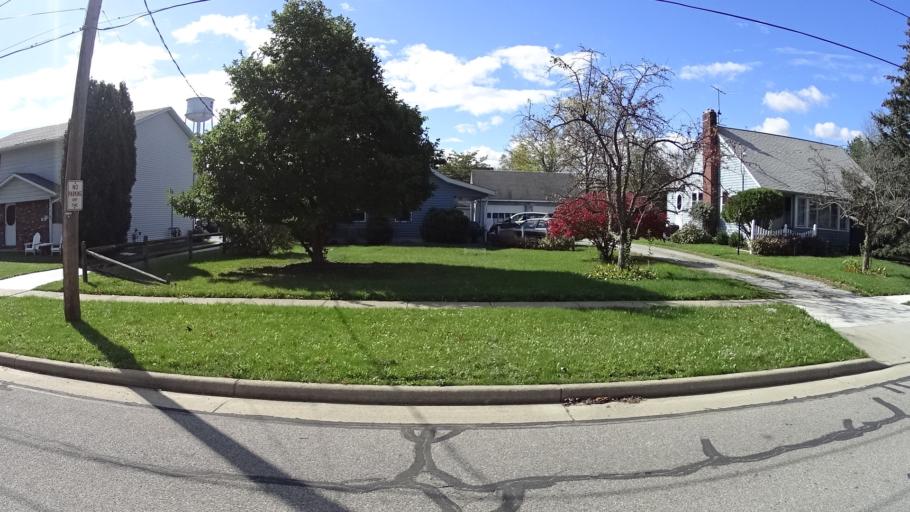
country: US
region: Ohio
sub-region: Lorain County
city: Grafton
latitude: 41.2742
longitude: -82.0554
